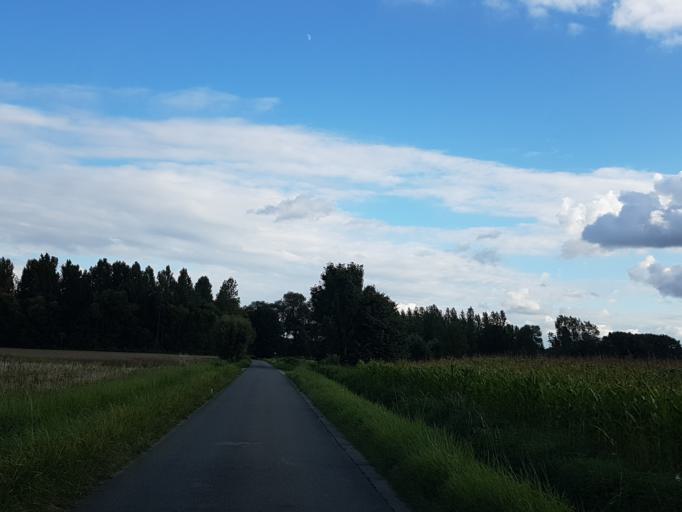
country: BE
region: Flanders
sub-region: Provincie Vlaams-Brabant
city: Kampenhout
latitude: 50.9299
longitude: 4.5948
